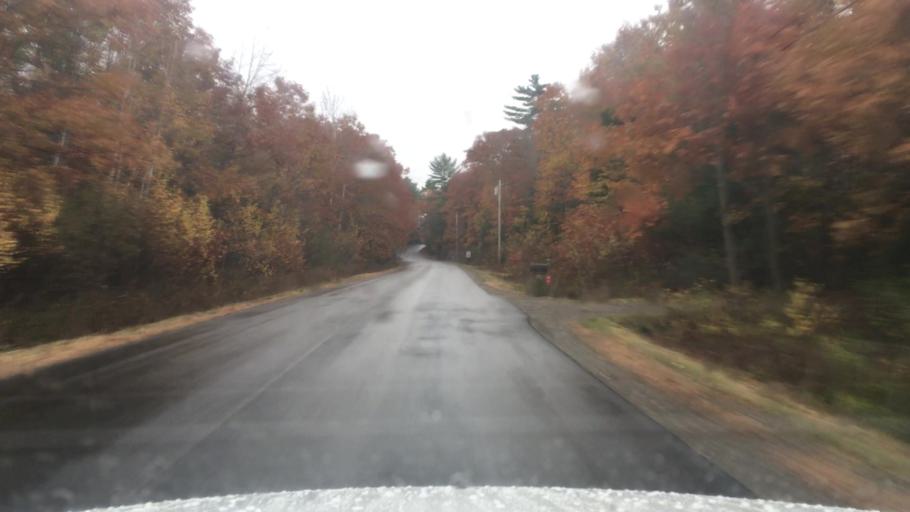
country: US
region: Maine
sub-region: Waldo County
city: Lincolnville
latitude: 44.3144
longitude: -69.0724
